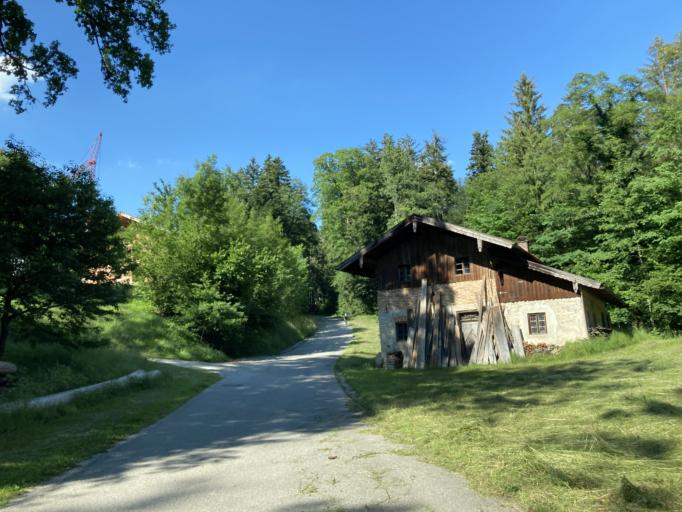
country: DE
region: Bavaria
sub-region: Upper Bavaria
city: Samerberg
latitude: 47.7516
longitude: 12.1998
